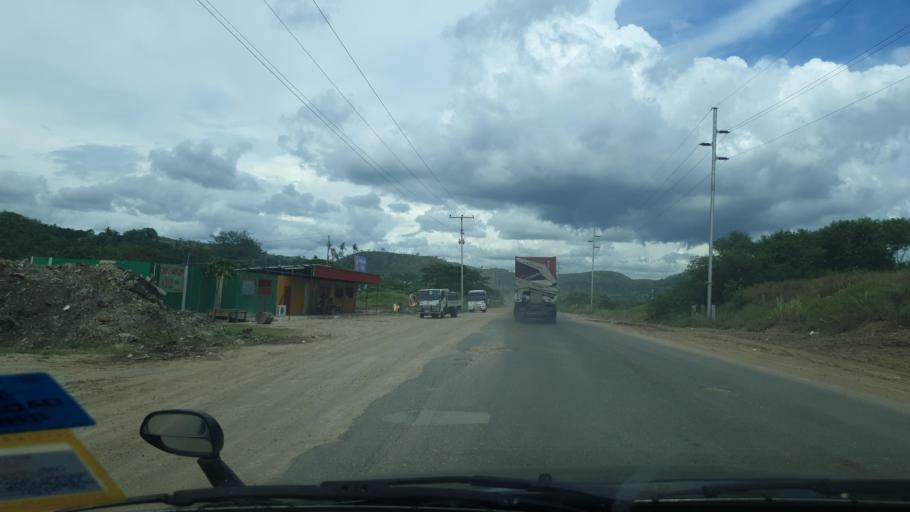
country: PG
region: National Capital
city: Port Moresby
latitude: -9.4178
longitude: 147.1197
